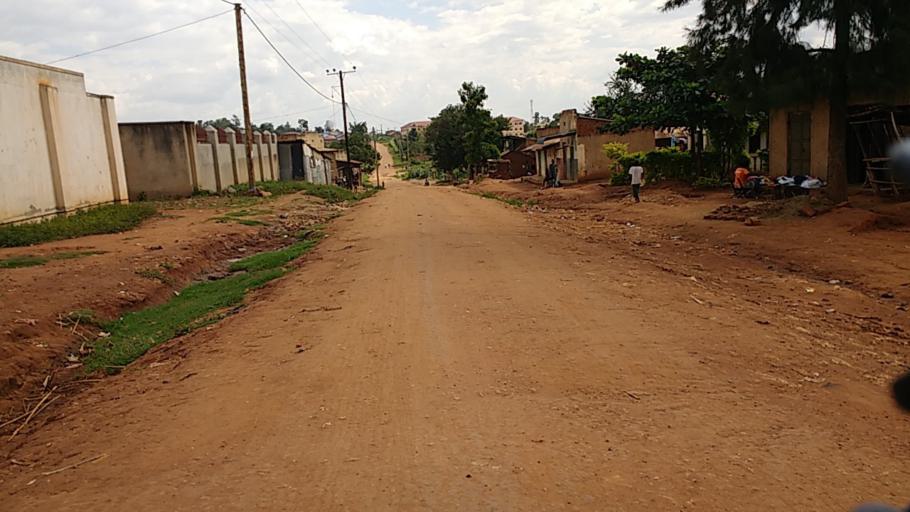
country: UG
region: Eastern Region
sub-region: Mbale District
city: Mbale
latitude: 1.0855
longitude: 34.1635
